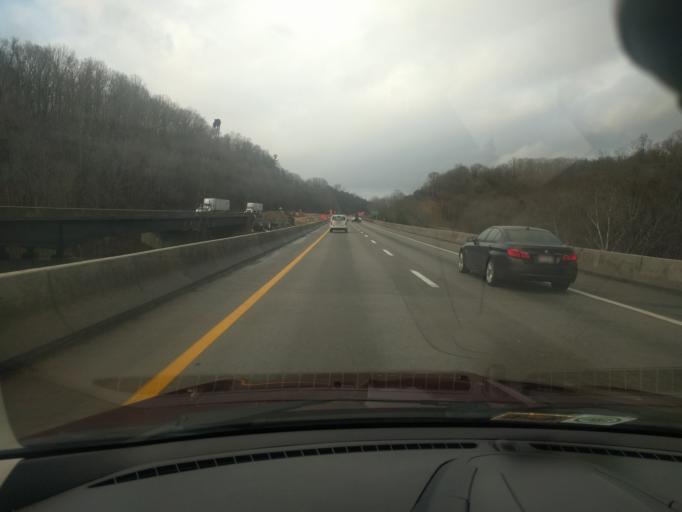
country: US
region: Virginia
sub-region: City of Radford
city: Radford
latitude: 37.0890
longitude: -80.5814
